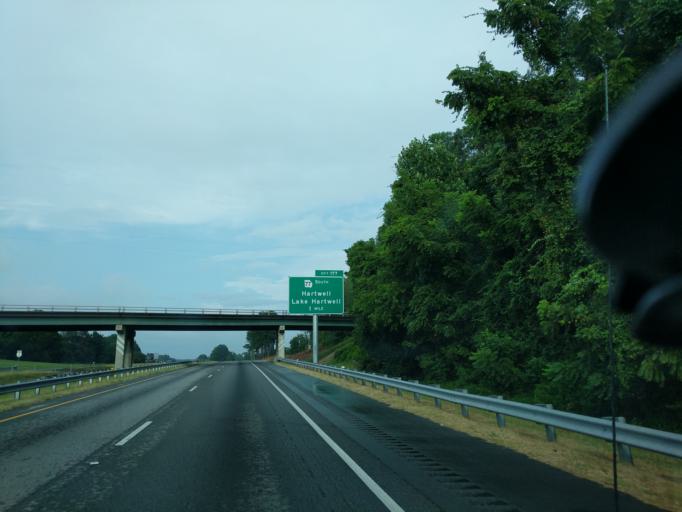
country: US
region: Georgia
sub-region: Franklin County
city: Gumlog
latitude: 34.4670
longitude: -83.0790
